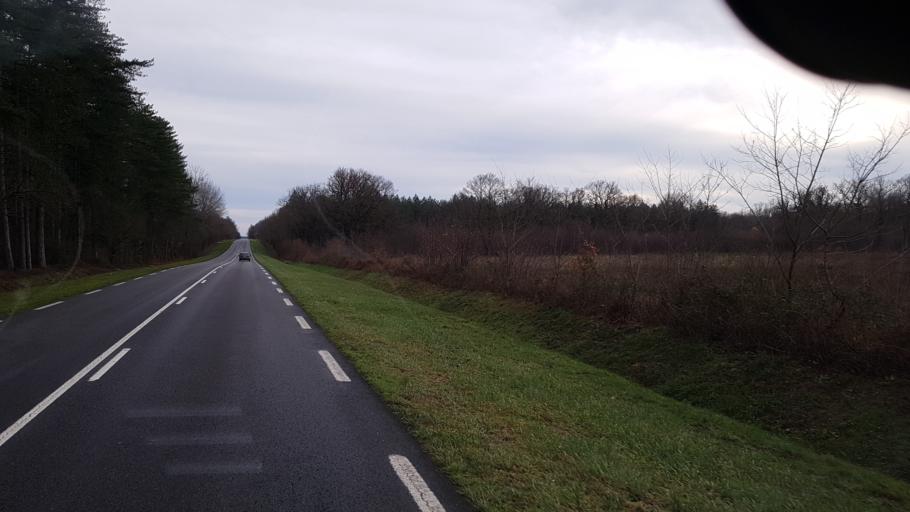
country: FR
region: Centre
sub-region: Departement du Loir-et-Cher
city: Lamotte-Beuvron
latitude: 47.6264
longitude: 2.0083
